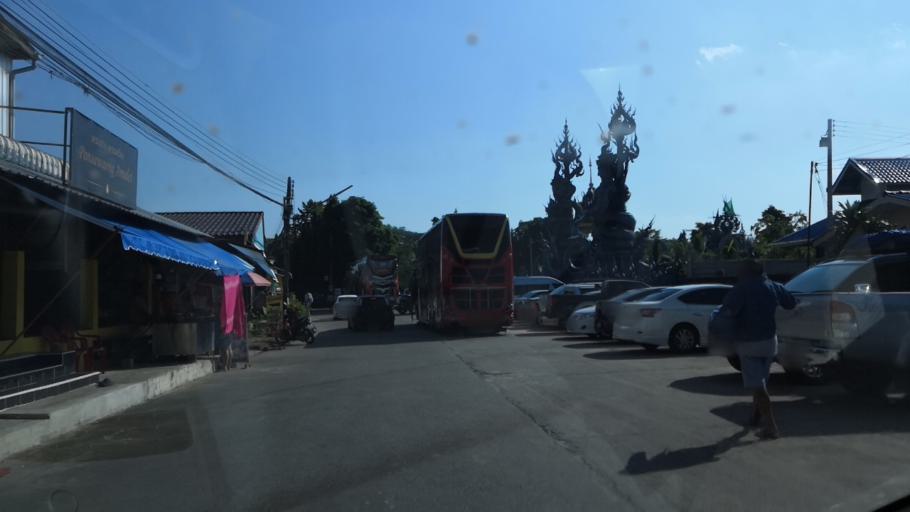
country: TH
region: Chiang Rai
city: Chiang Rai
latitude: 19.9240
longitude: 99.8423
